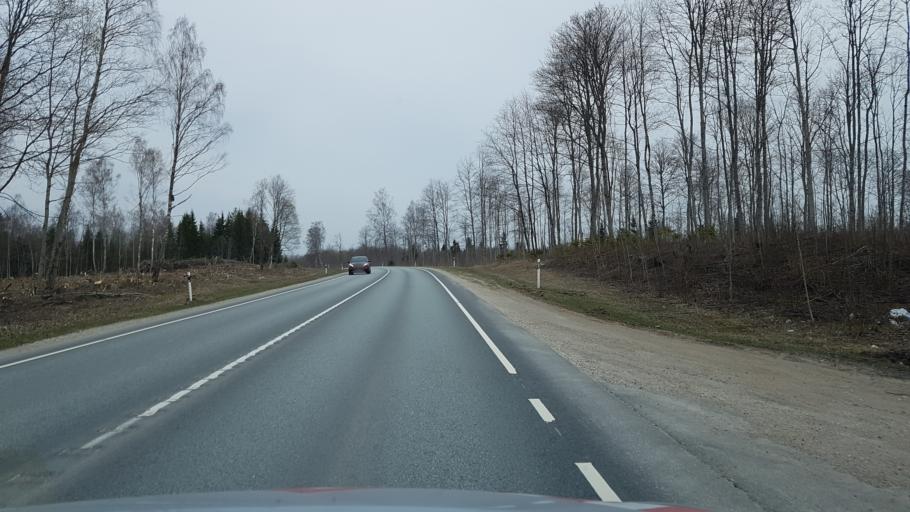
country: EE
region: Laeaene-Virumaa
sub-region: Kadrina vald
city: Kadrina
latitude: 59.3056
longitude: 26.0734
